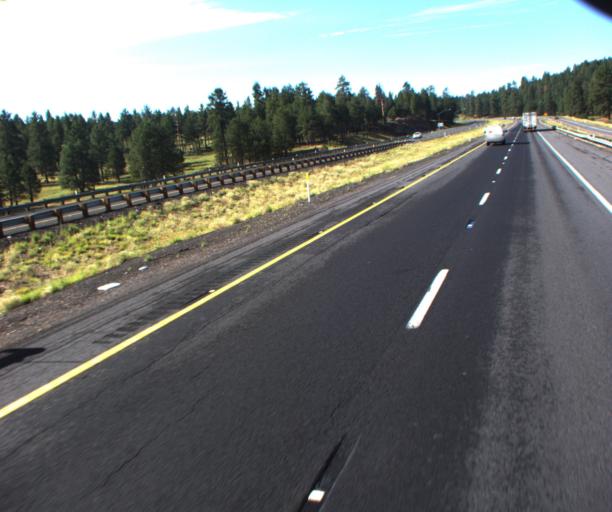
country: US
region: Arizona
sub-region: Coconino County
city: Kachina Village
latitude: 35.0896
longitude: -111.6863
